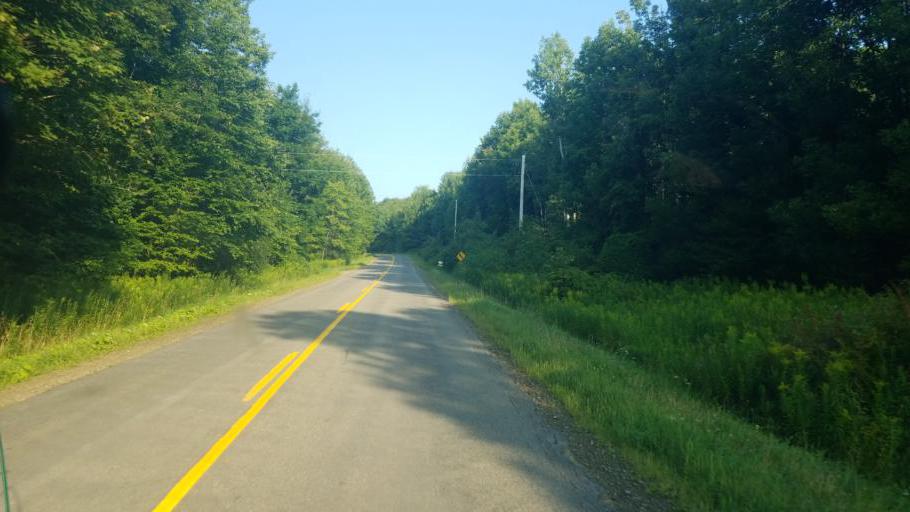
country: US
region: Pennsylvania
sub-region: Tioga County
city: Westfield
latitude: 42.0656
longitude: -77.6284
